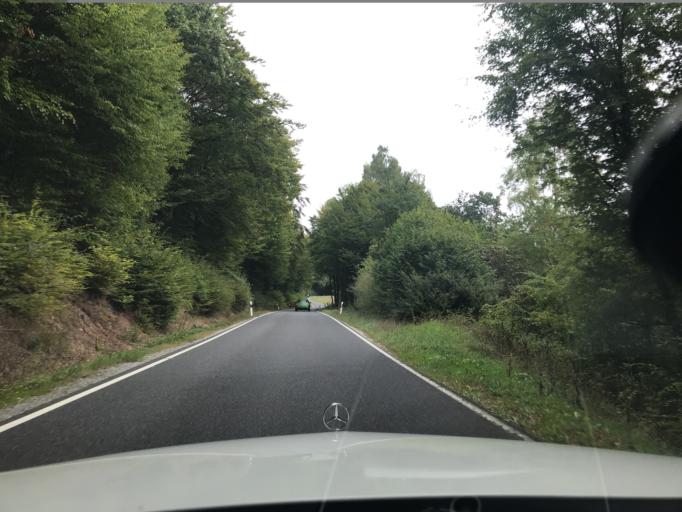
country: DE
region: Hesse
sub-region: Regierungsbezirk Kassel
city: Helsa
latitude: 51.2458
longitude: 9.7028
